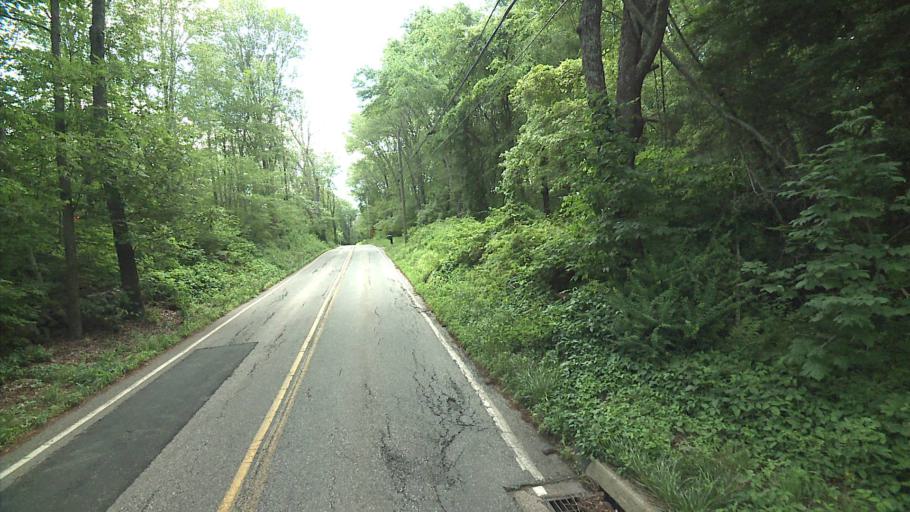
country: US
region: Connecticut
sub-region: New London County
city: Old Mystic
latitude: 41.4378
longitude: -71.9160
